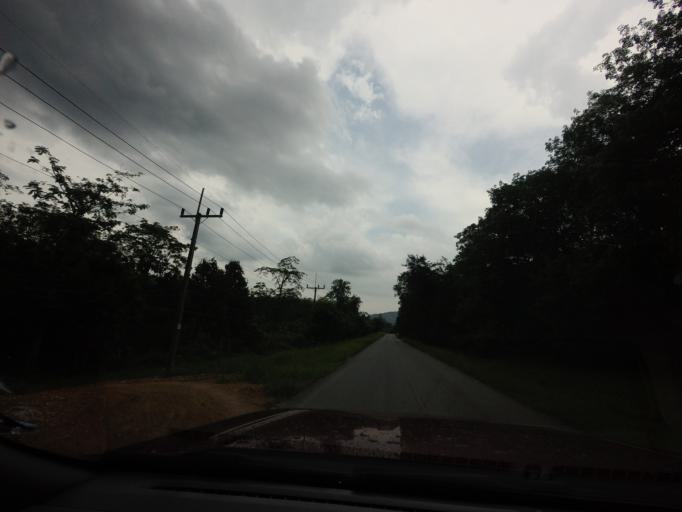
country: TH
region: Yala
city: Ban Nang Sata
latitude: 6.2171
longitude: 101.2315
